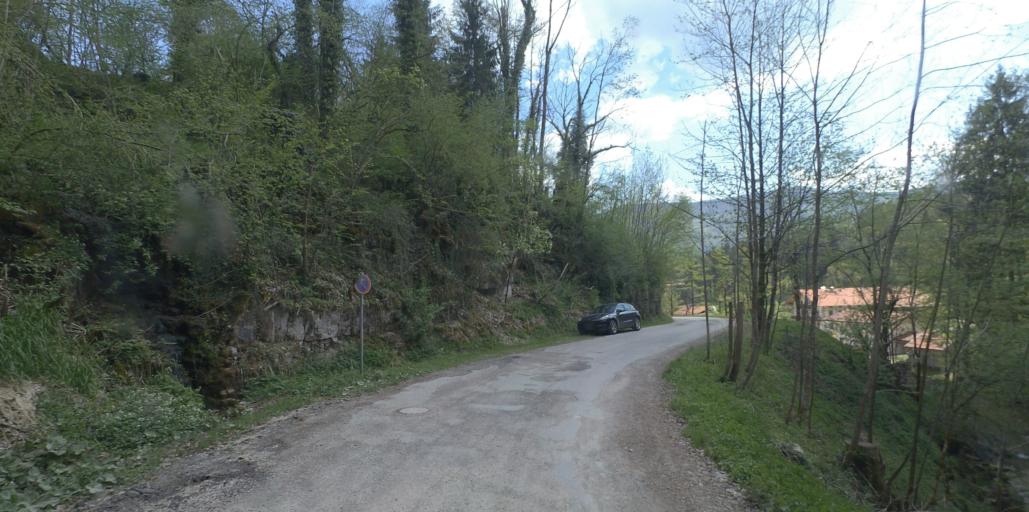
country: DE
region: Bavaria
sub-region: Upper Bavaria
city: Schleching
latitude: 47.7287
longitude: 12.3943
